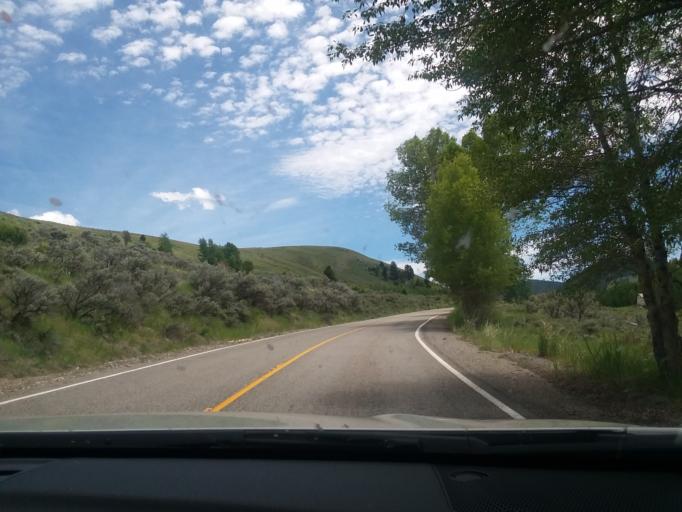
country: US
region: Wyoming
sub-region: Teton County
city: Jackson
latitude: 43.4957
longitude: -110.7746
